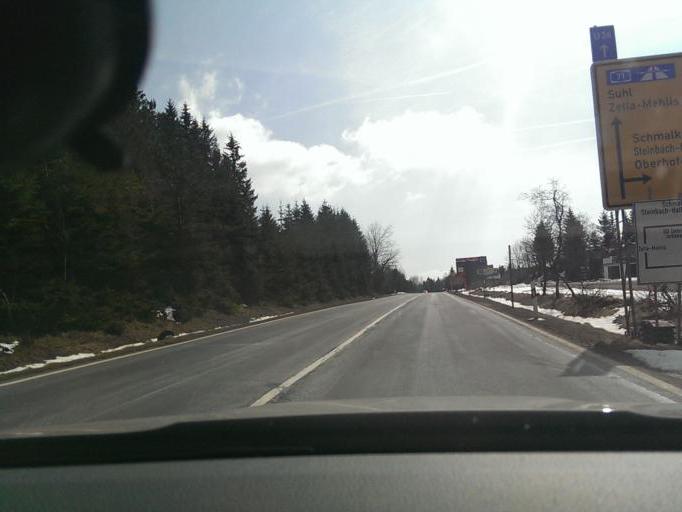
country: DE
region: Thuringia
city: Oberhof
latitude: 50.7071
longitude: 10.7331
